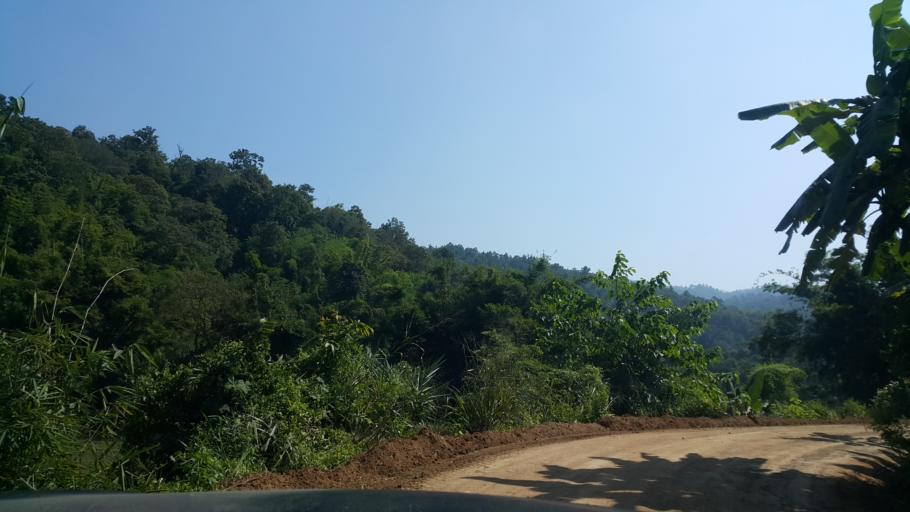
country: TH
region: Chiang Mai
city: Samoeng
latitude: 18.9297
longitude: 98.6150
